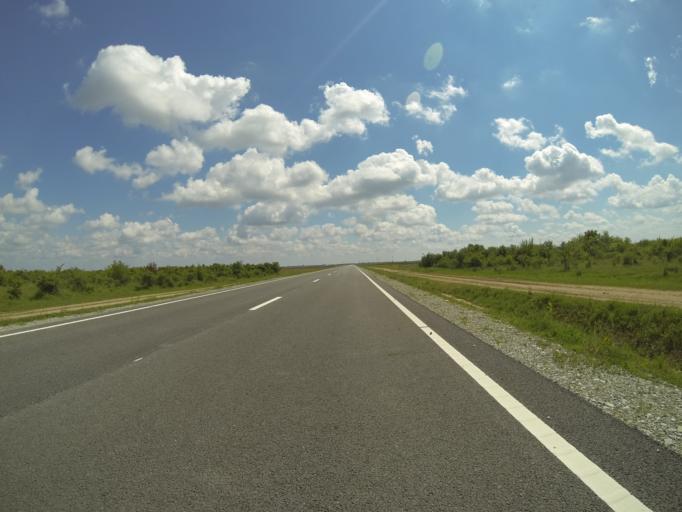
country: RO
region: Dolj
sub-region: Comuna Carcea
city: Carcea
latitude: 44.2786
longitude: 23.9084
